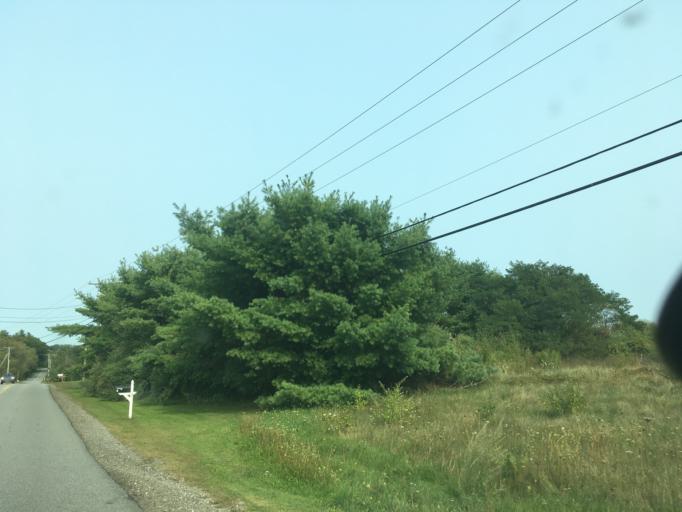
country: US
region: New Hampshire
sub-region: Rockingham County
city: Stratham Station
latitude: 42.9983
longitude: -70.8863
